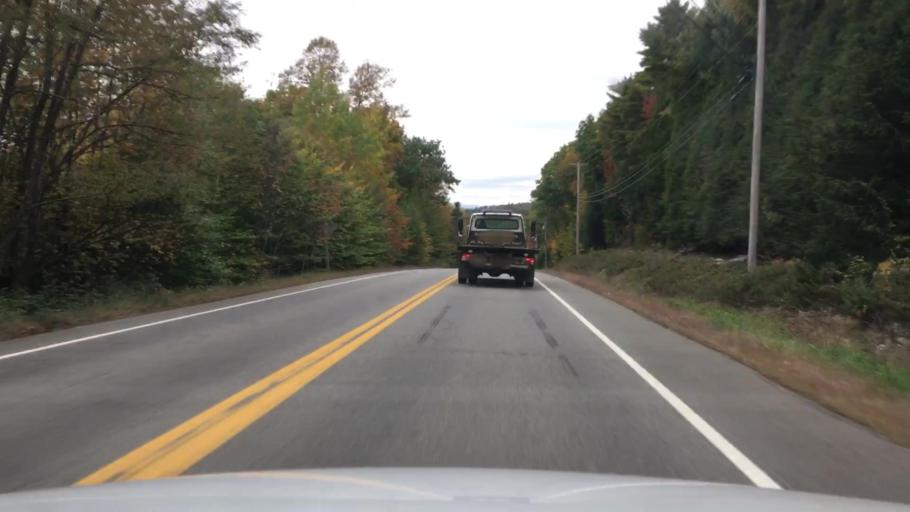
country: US
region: Maine
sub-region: Kennebec County
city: Oakland
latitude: 44.5595
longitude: -69.7439
